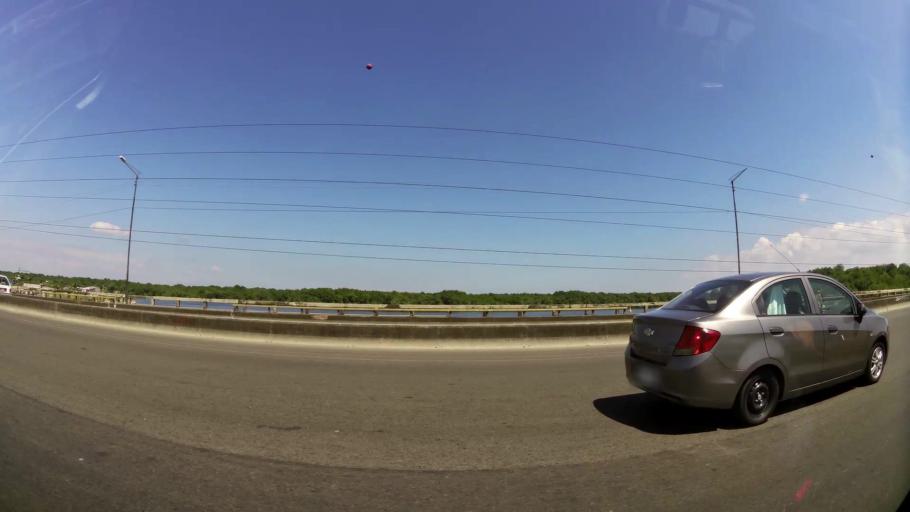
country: EC
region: Guayas
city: Guayaquil
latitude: -2.2319
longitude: -79.9469
